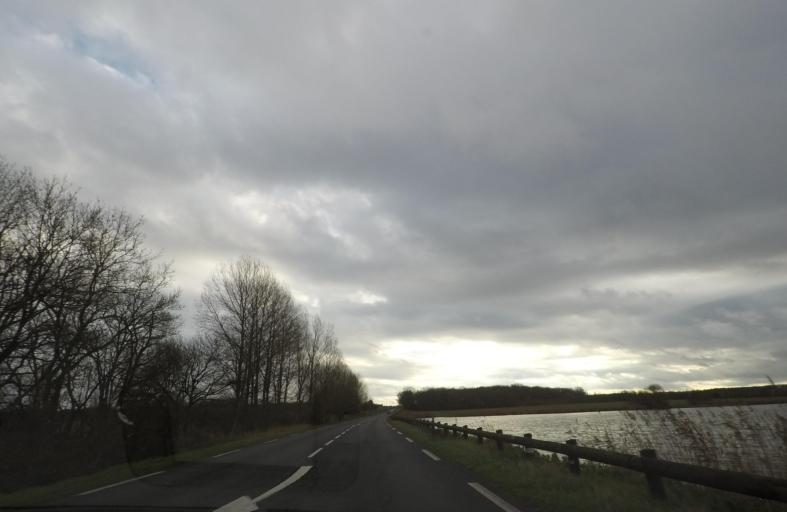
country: FR
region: Centre
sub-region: Departement du Loir-et-Cher
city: Soings-en-Sologne
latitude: 47.4361
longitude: 1.5570
